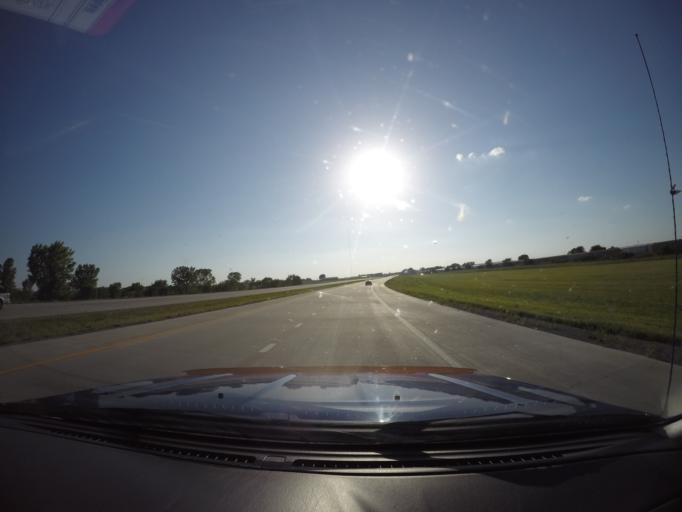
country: US
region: Kansas
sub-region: Shawnee County
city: Topeka
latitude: 39.0906
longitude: -95.7620
